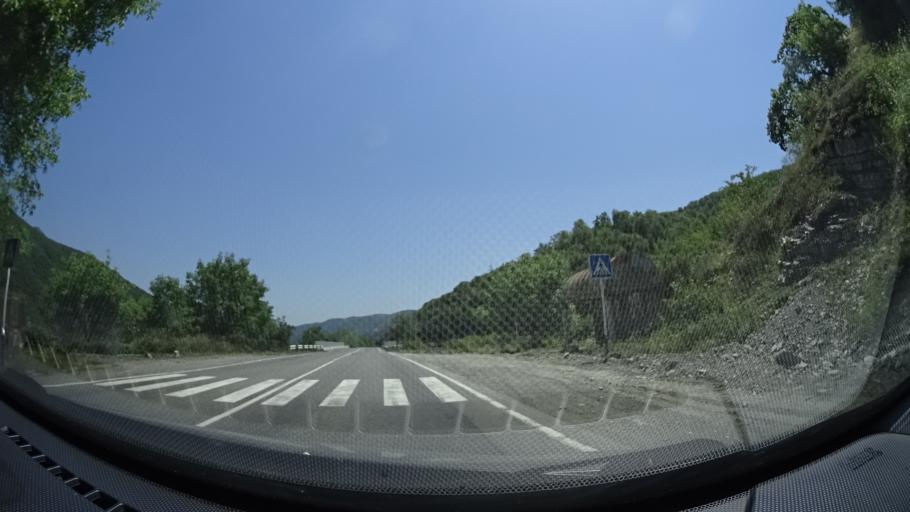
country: GE
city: Zhinvali
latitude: 42.1785
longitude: 44.6858
